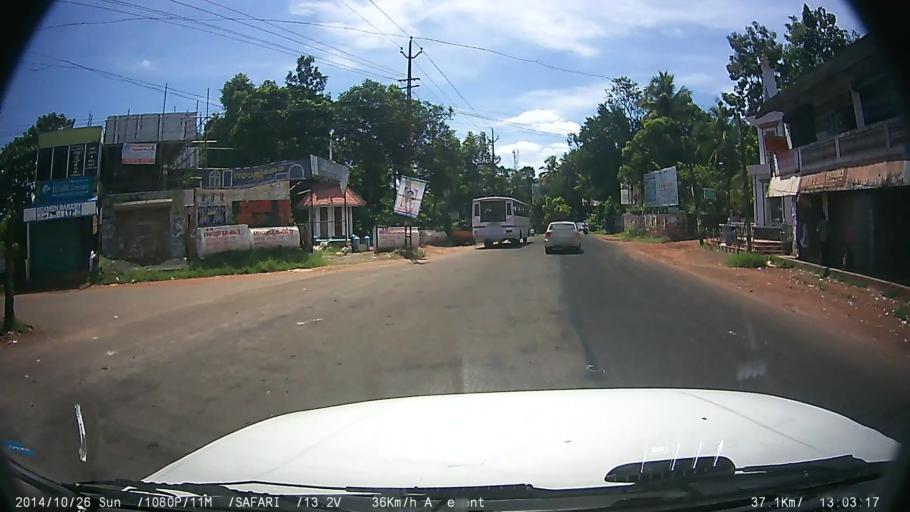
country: IN
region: Kerala
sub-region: Kottayam
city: Changanacheri
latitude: 9.4960
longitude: 76.5248
